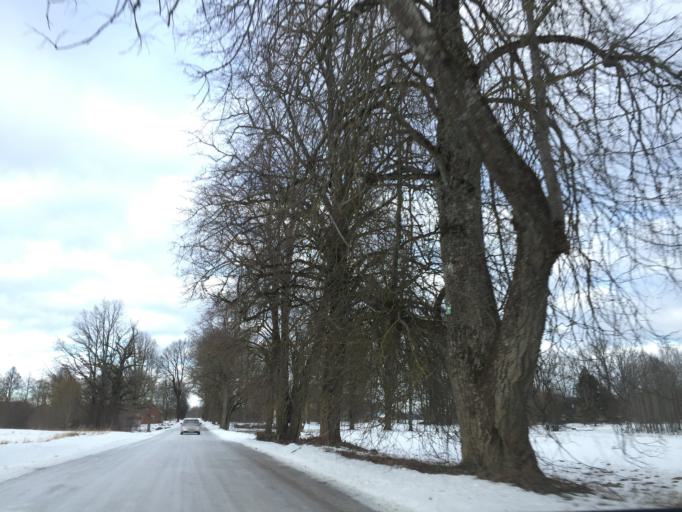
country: LV
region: Lielvarde
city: Lielvarde
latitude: 56.5634
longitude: 24.7345
